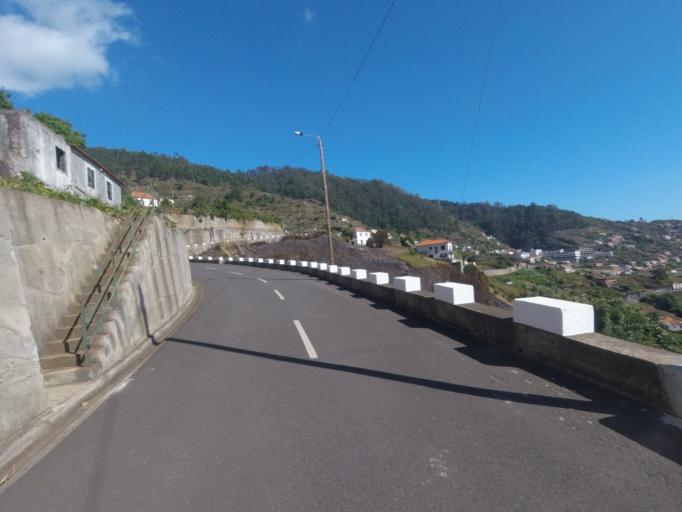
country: PT
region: Madeira
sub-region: Ribeira Brava
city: Campanario
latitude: 32.6773
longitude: -17.0247
